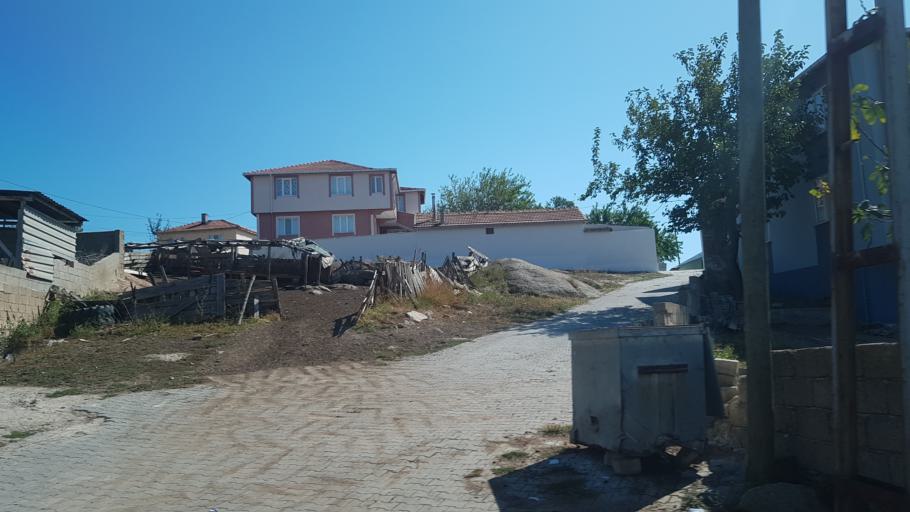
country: TR
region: Kirklareli
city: Kirklareli
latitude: 41.7736
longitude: 27.2265
